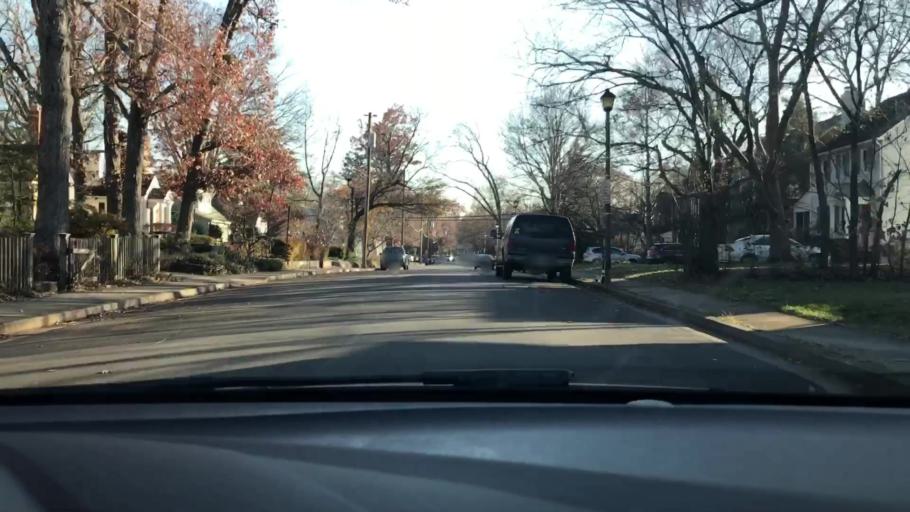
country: US
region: Virginia
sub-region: Arlington County
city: Arlington
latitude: 38.8801
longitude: -77.0997
